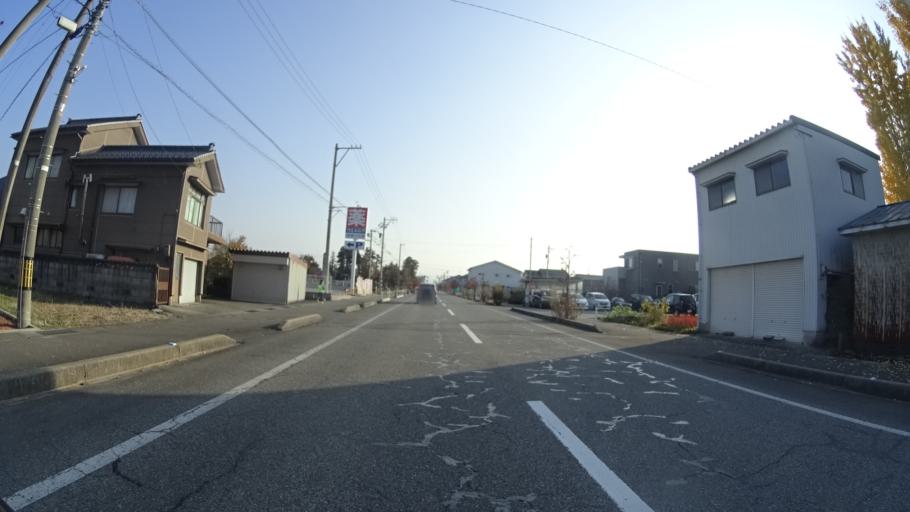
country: JP
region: Toyama
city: Kamiichi
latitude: 36.6631
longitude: 137.3123
